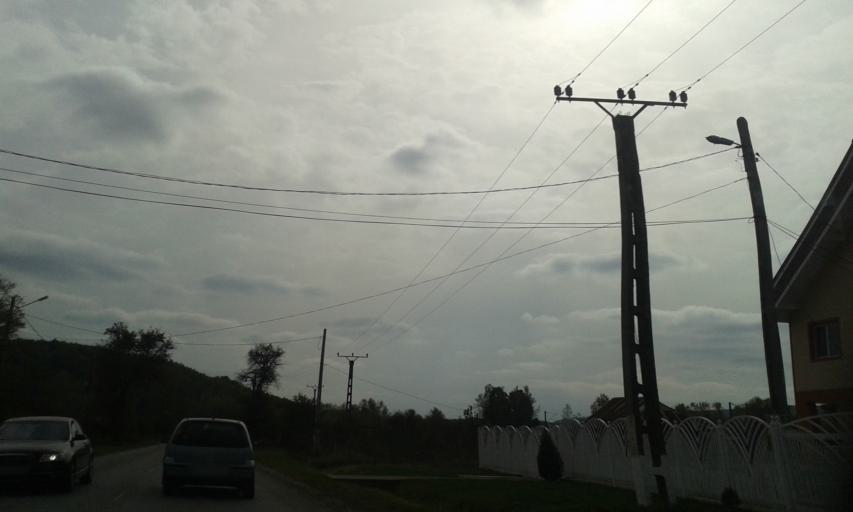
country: RO
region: Gorj
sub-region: Comuna Targu Carbunesti
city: Pojogeni
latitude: 44.9781
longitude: 23.5015
